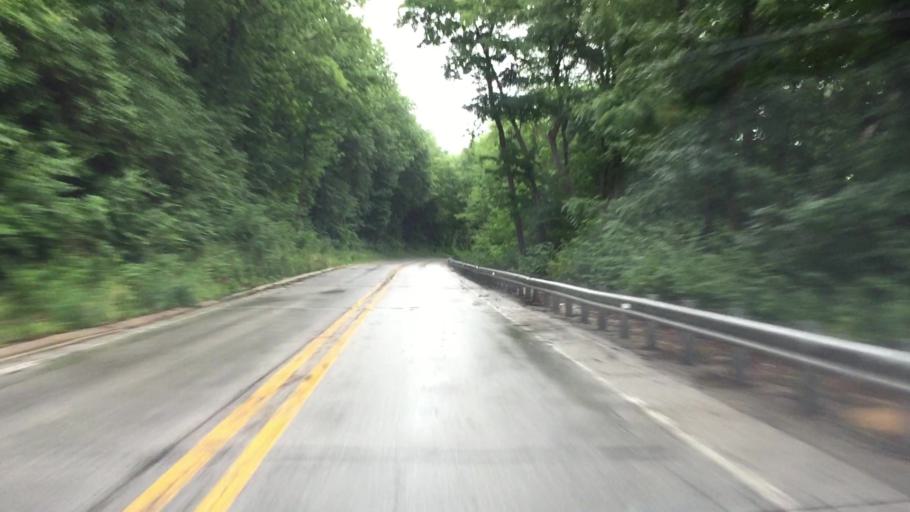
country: US
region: Illinois
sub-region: Hancock County
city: Hamilton
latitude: 40.4722
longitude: -91.3594
